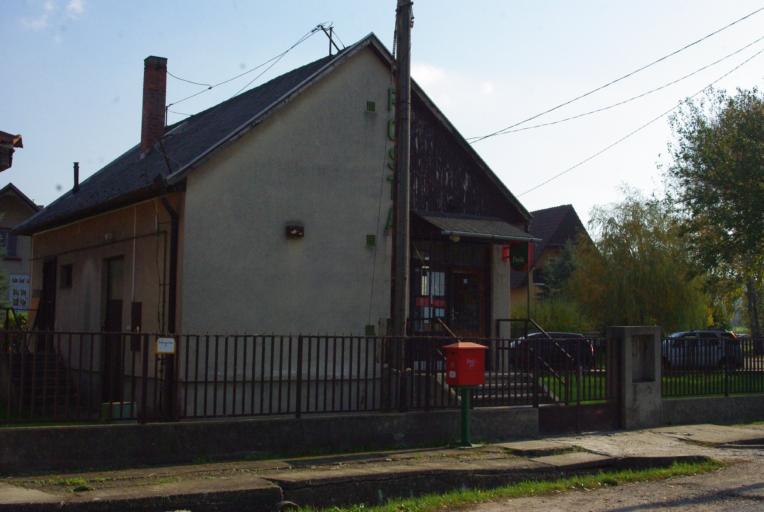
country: HU
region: Komarom-Esztergom
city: Piliscsev
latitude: 47.6761
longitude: 18.8198
